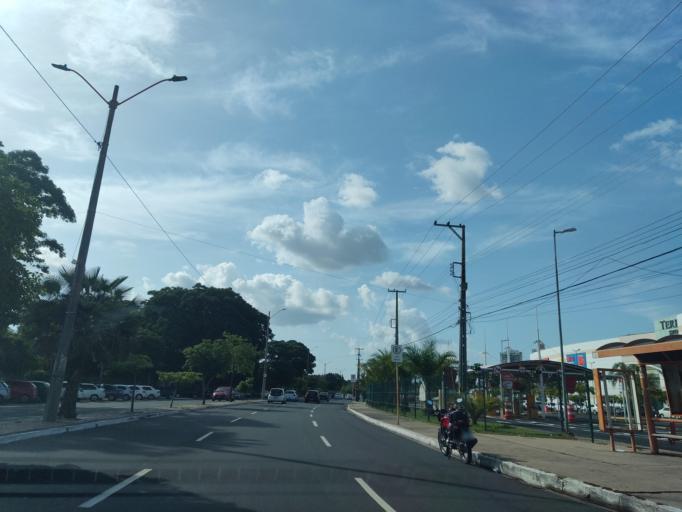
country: BR
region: Piaui
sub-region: Teresina
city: Teresina
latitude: -5.0859
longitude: -42.7908
